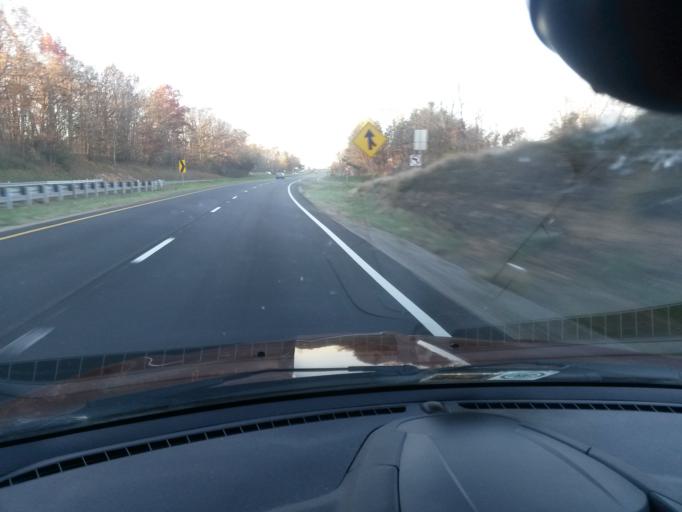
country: US
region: Virginia
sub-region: Franklin County
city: Henry Fork
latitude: 36.9633
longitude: -79.8739
